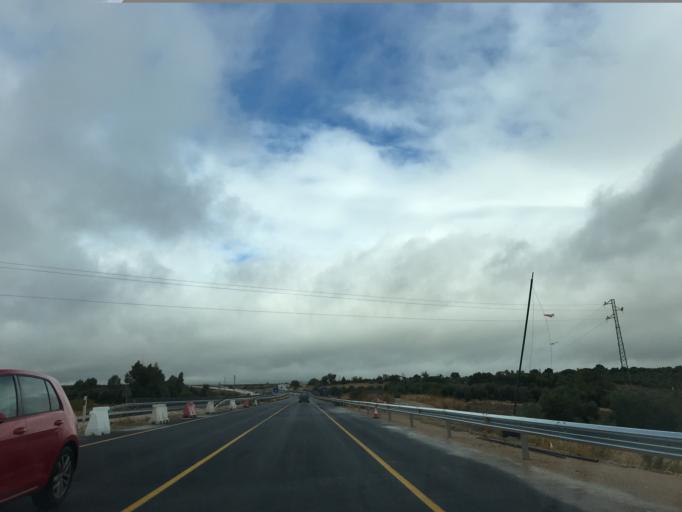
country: ES
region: Andalusia
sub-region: Provincia de Jaen
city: Ubeda
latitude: 38.0200
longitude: -3.4099
